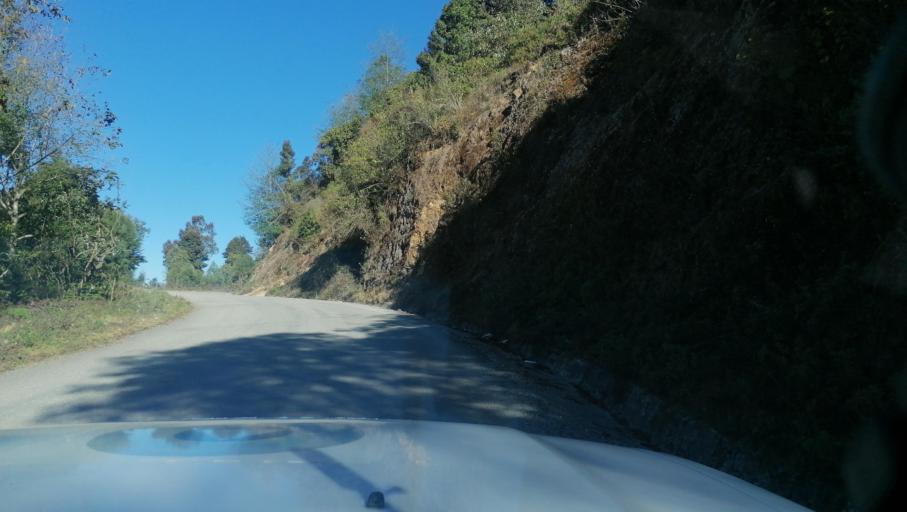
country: MX
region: Chiapas
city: Motozintla de Mendoza
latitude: 15.2668
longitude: -92.2263
